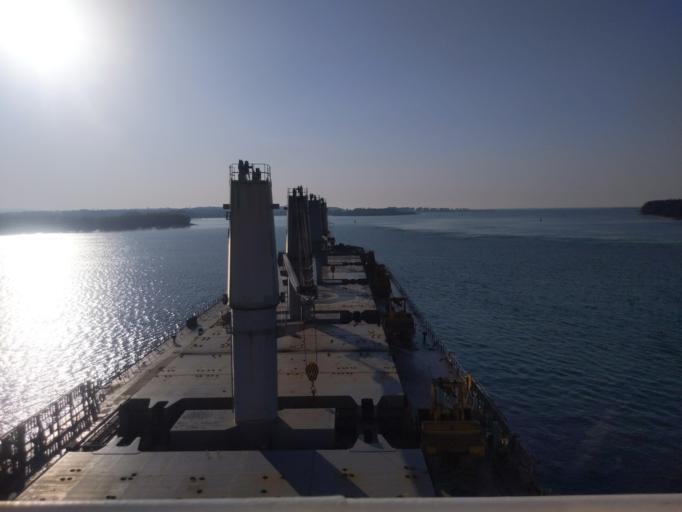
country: ZA
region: KwaZulu-Natal
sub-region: uThungulu District Municipality
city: Richards Bay
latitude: -28.8009
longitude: 32.0587
